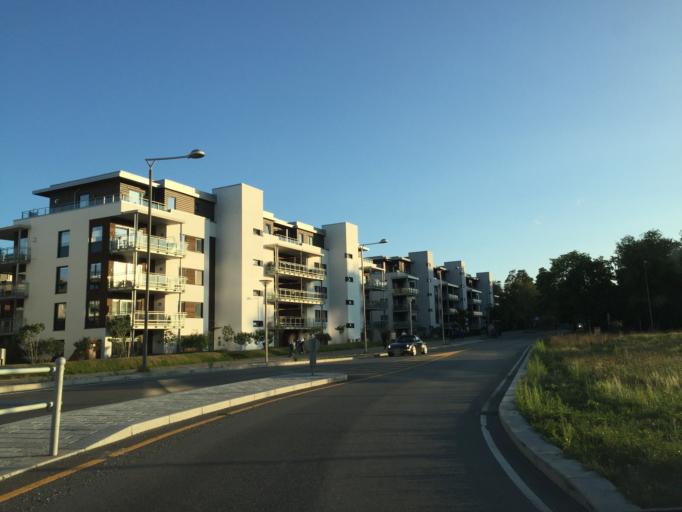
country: NO
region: Akershus
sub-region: Baerum
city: Lysaker
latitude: 59.8928
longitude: 10.6295
